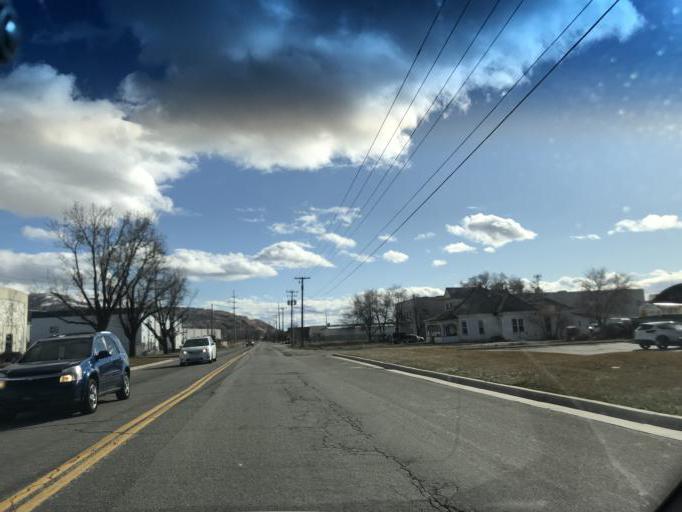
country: US
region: Utah
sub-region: Davis County
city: North Salt Lake
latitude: 40.8608
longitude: -111.9119
